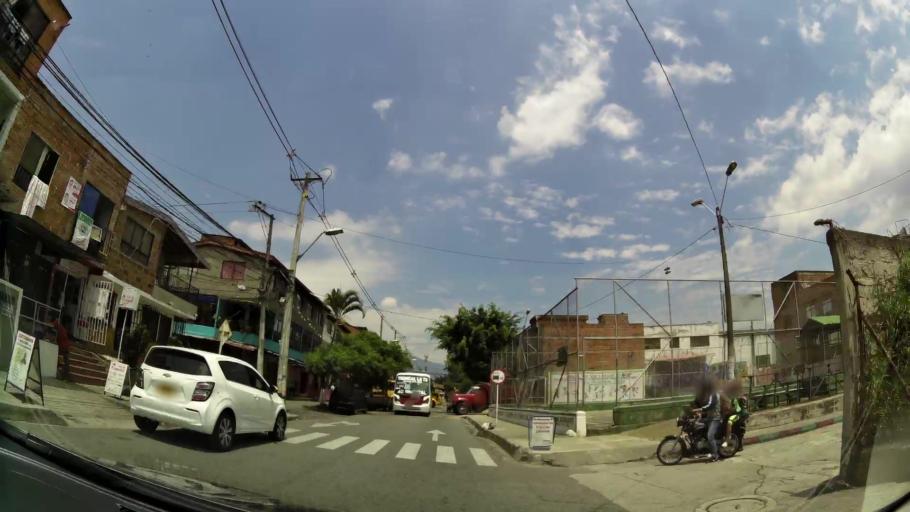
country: CO
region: Antioquia
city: Bello
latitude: 6.2983
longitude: -75.5756
